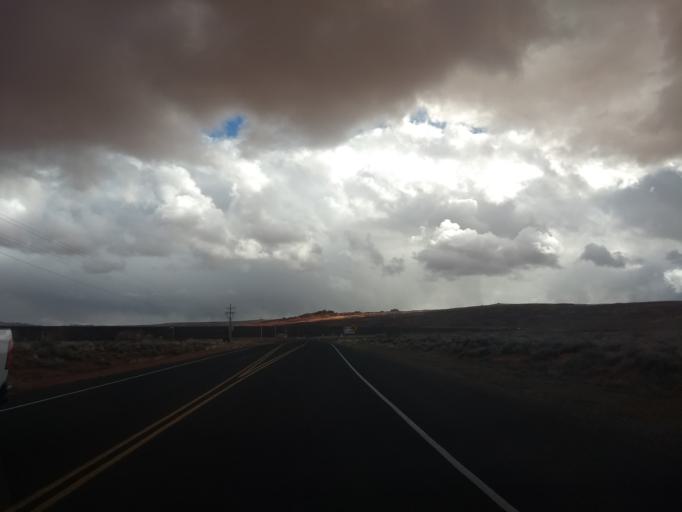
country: US
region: Utah
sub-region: Washington County
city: Hurricane
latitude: 37.1190
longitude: -113.3920
